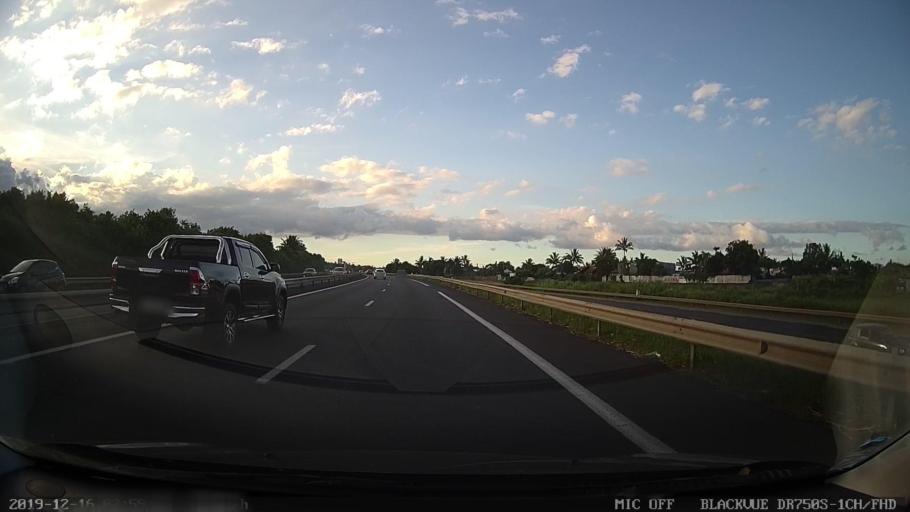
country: RE
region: Reunion
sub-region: Reunion
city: Sainte-Suzanne
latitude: -20.9187
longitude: 55.6246
